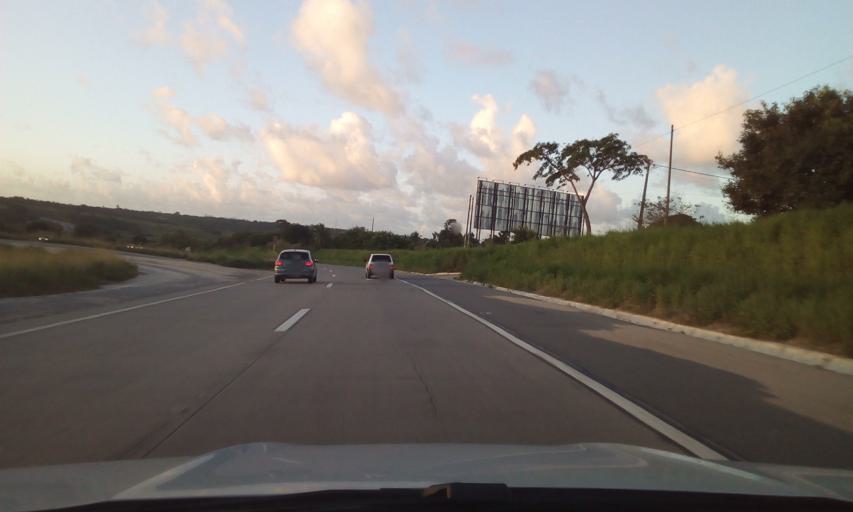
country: BR
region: Pernambuco
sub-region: Itapissuma
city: Itapissuma
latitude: -7.7005
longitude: -34.9219
